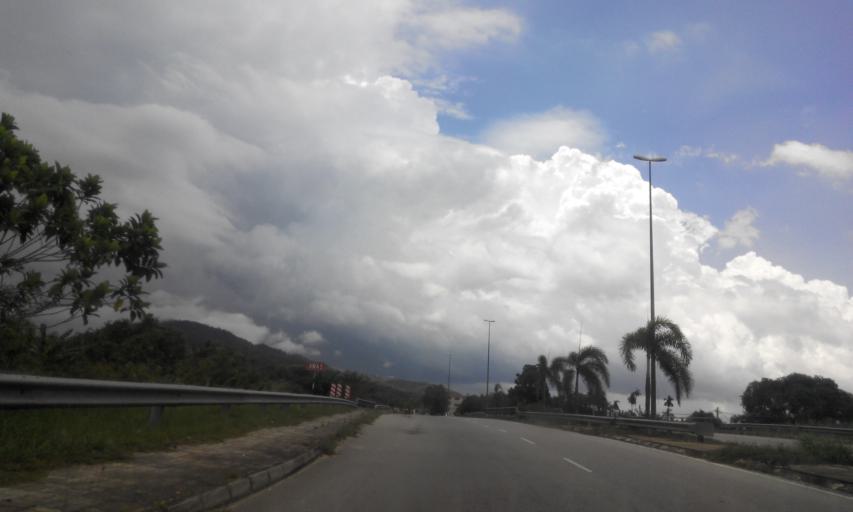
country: MY
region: Perak
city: Parit Buntar
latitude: 5.1277
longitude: 100.5053
